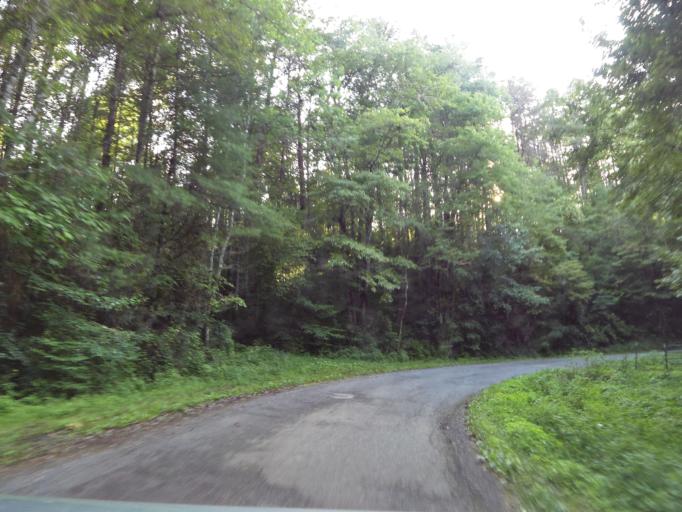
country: US
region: Tennessee
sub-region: Blount County
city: Maryville
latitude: 35.6075
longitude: -83.9422
